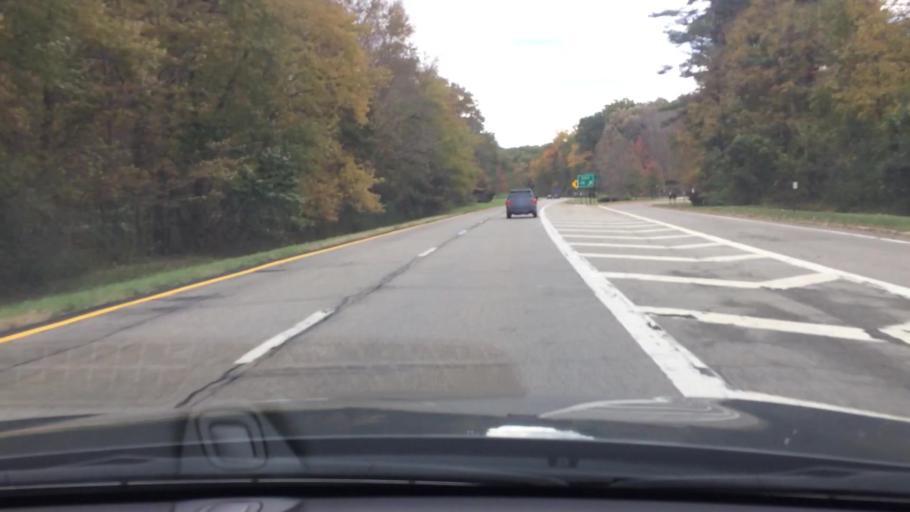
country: US
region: New York
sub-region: Dutchess County
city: Hillside Lake
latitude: 41.6337
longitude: -73.7823
